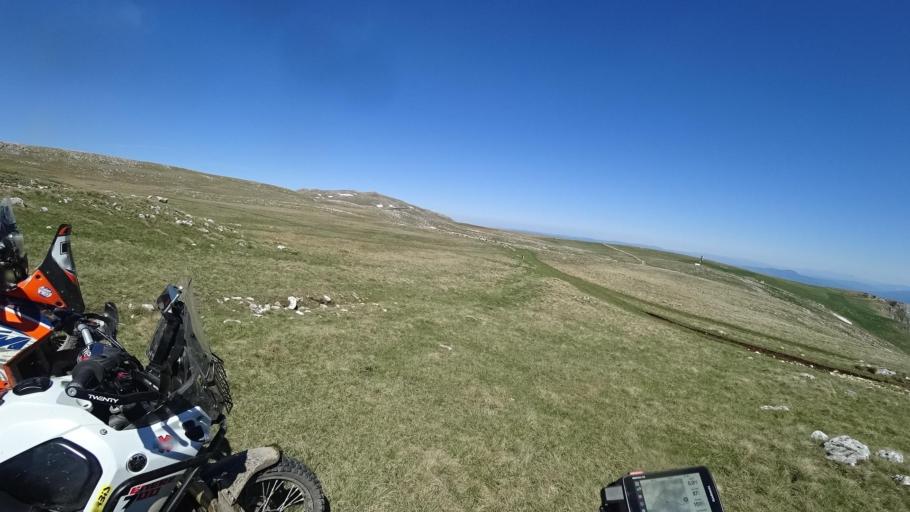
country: BA
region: Federation of Bosnia and Herzegovina
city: Travnik
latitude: 44.2769
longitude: 17.6361
